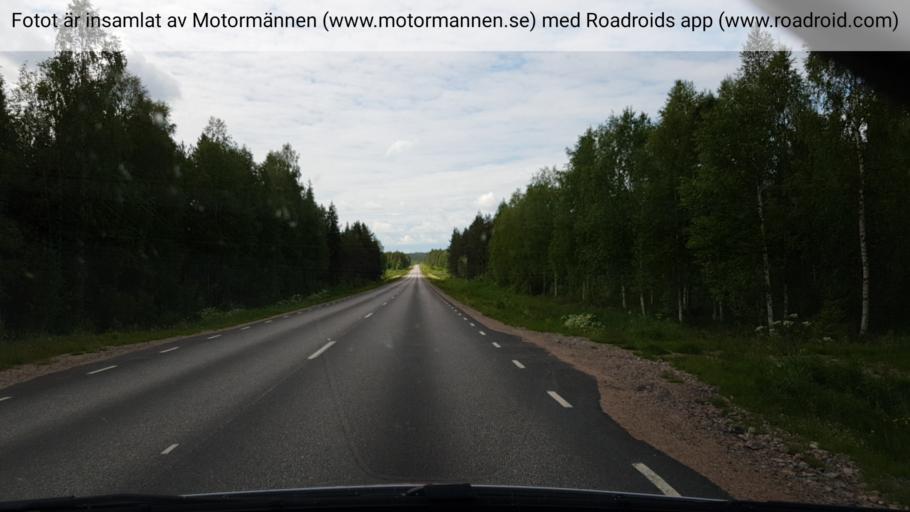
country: SE
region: Norrbotten
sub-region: Overtornea Kommun
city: OEvertornea
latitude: 66.5237
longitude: 23.7633
